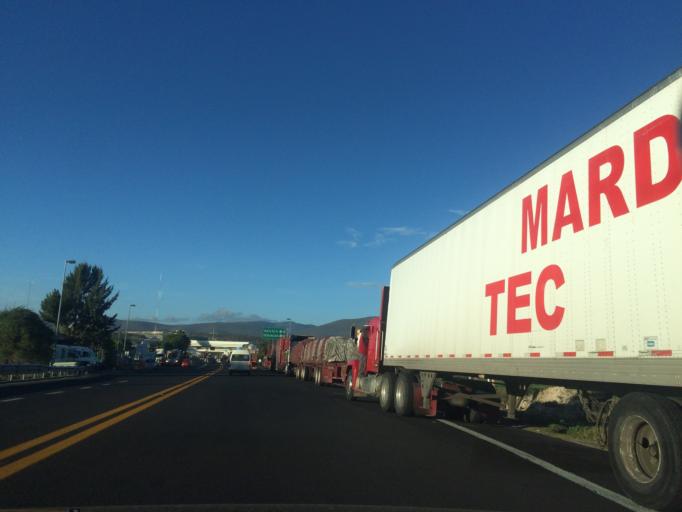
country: MX
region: Puebla
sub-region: Santiago Miahuatlan
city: San Jose Monte Chiquito
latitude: 18.4897
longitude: -97.4557
